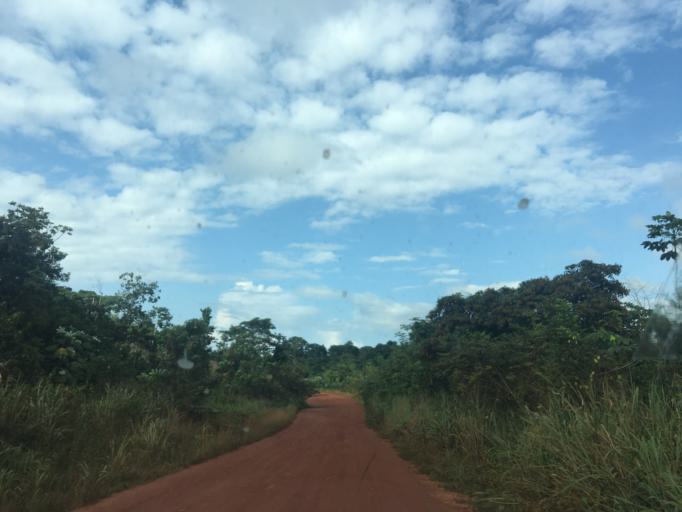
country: GH
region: Western
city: Wassa-Akropong
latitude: 5.9545
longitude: -2.4354
